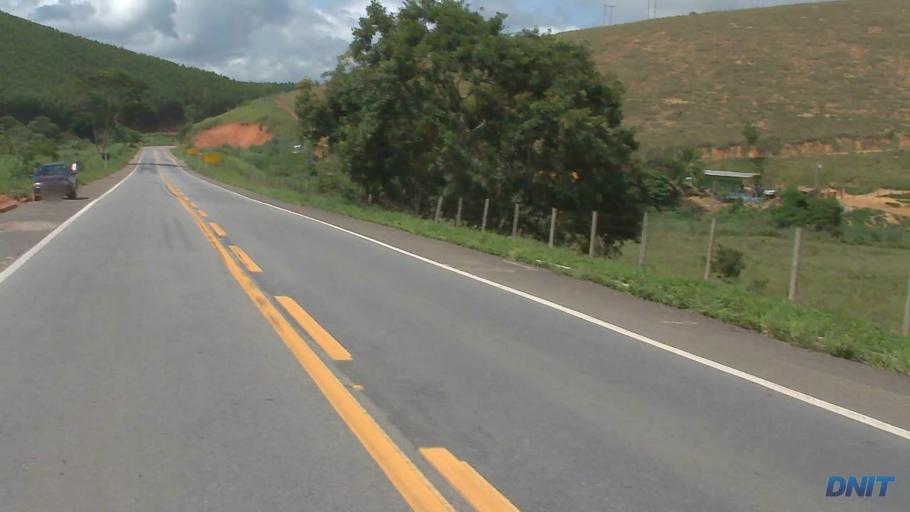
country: BR
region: Minas Gerais
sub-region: Belo Oriente
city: Belo Oriente
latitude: -19.1127
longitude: -42.2034
